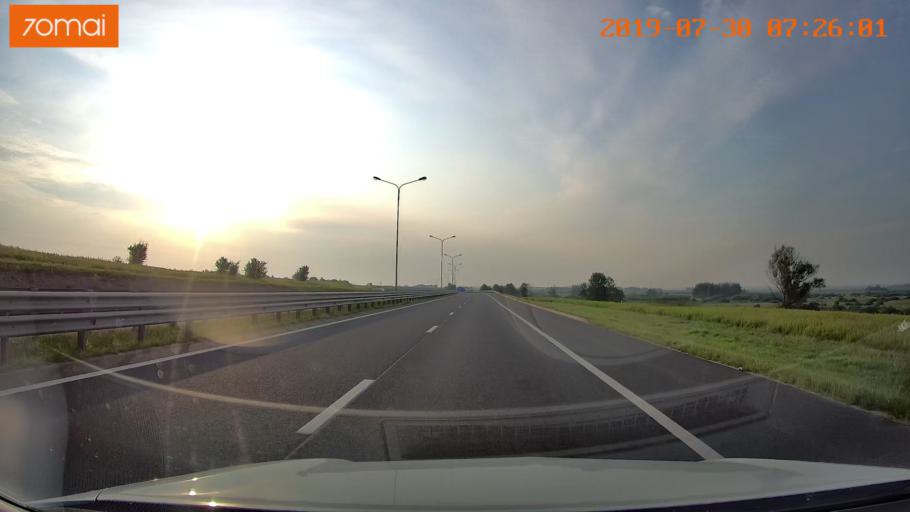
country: RU
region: Kaliningrad
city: Gvardeysk
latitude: 54.6841
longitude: 20.8498
